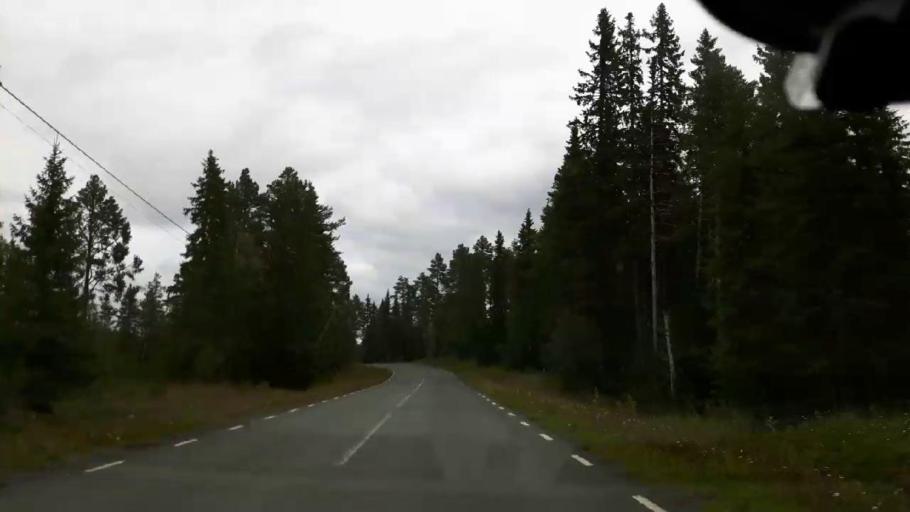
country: SE
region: Jaemtland
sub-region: Krokoms Kommun
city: Valla
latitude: 63.6643
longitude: 13.8557
